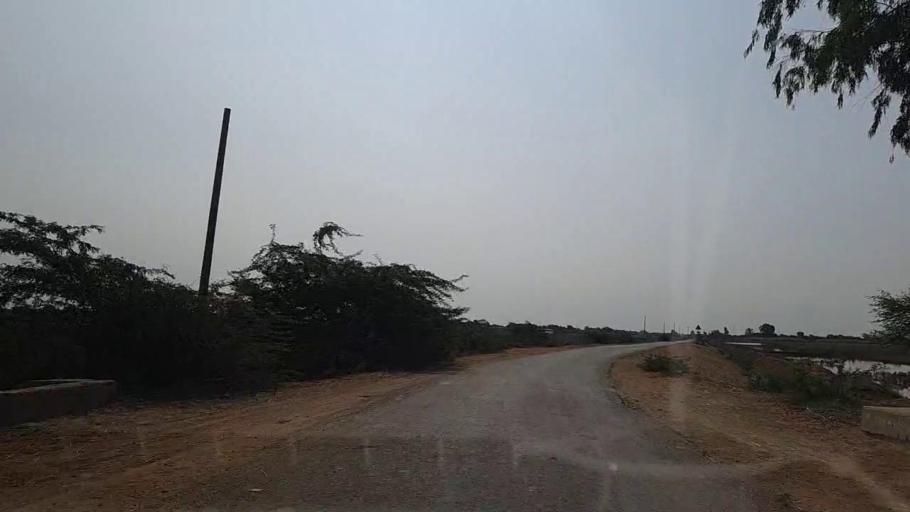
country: PK
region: Sindh
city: Chuhar Jamali
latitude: 24.3102
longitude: 67.9388
